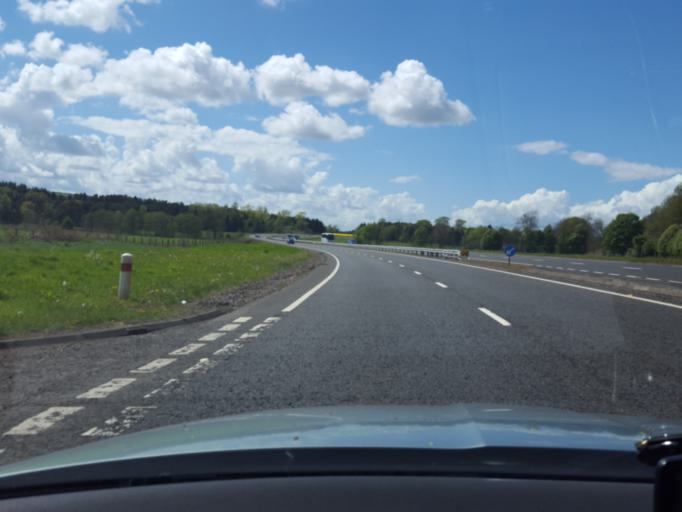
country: GB
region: Scotland
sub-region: Angus
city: Letham
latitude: 56.7196
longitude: -2.7605
